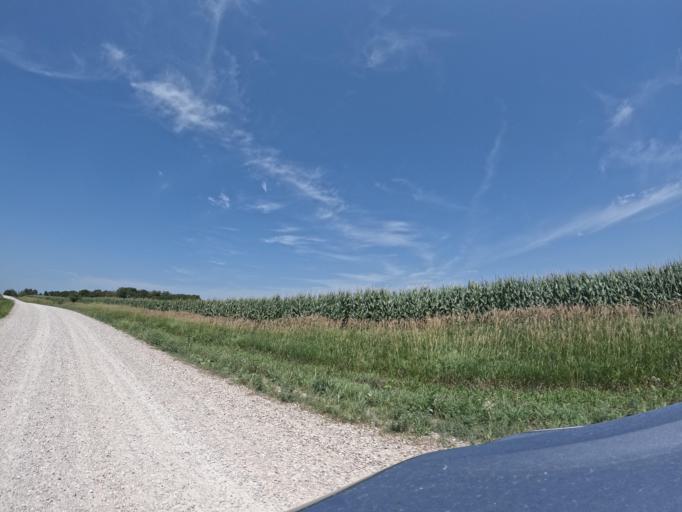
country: US
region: Iowa
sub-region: Henry County
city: Mount Pleasant
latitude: 40.9116
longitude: -91.6552
